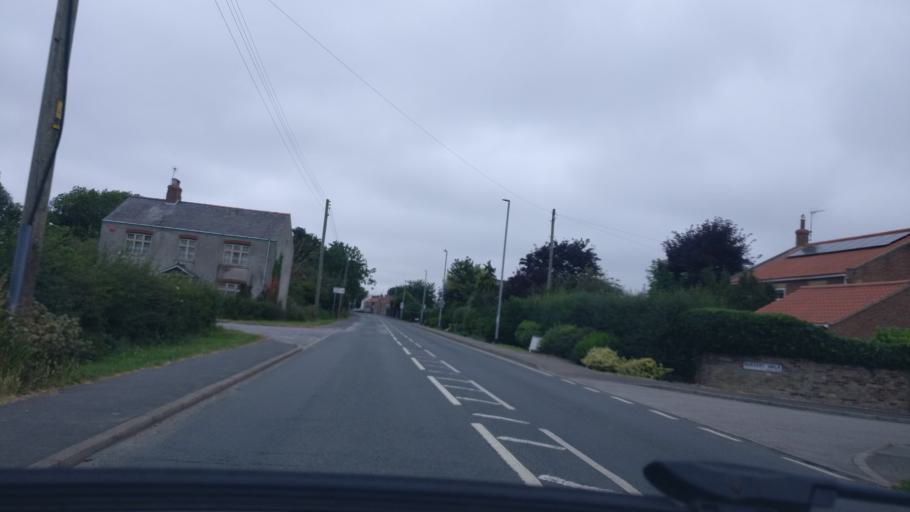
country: GB
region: England
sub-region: East Riding of Yorkshire
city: Leven
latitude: 53.8874
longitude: -0.3159
